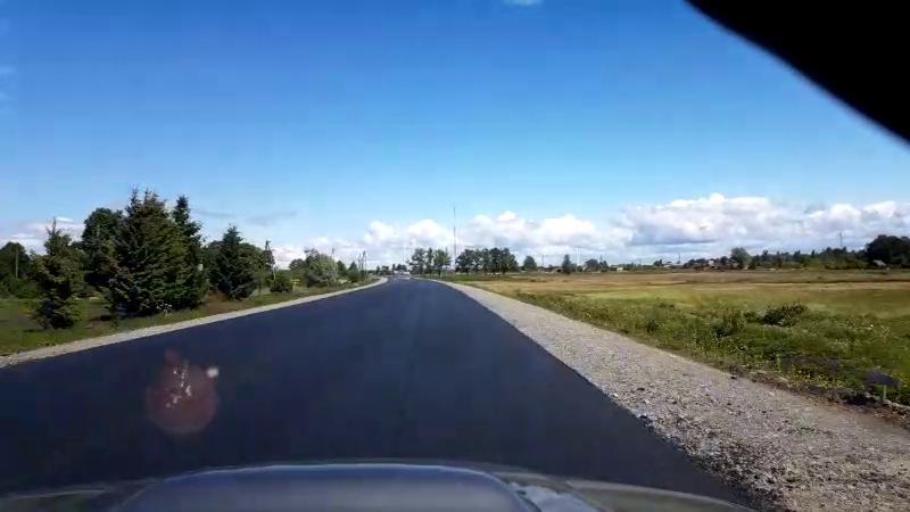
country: LV
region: Salacgrivas
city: Ainazi
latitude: 57.8576
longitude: 24.3658
